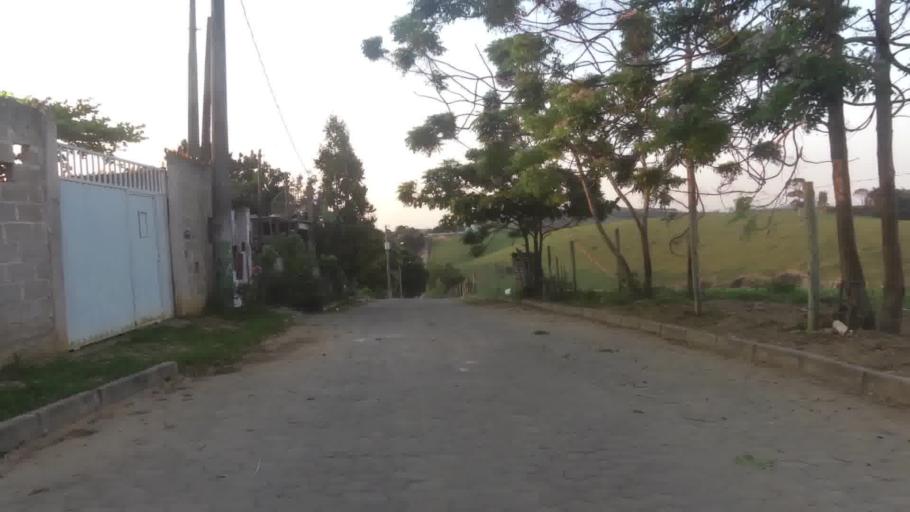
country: BR
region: Espirito Santo
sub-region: Piuma
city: Piuma
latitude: -20.8272
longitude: -40.7186
